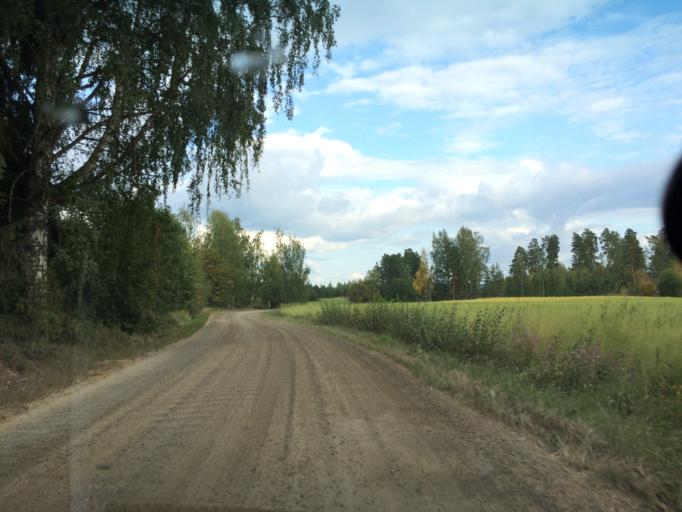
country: FI
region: Pirkanmaa
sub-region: Tampere
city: Luopioinen
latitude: 61.2612
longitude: 24.7047
